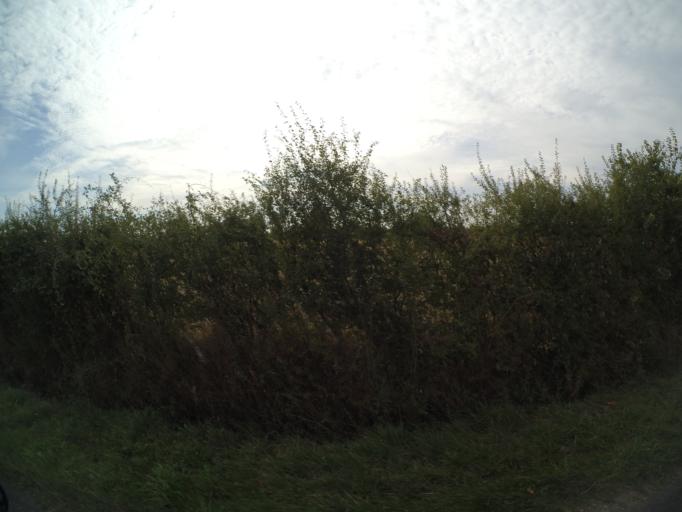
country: FR
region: Pays de la Loire
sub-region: Departement de Maine-et-Loire
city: Vihiers
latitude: 47.2077
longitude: -0.5370
